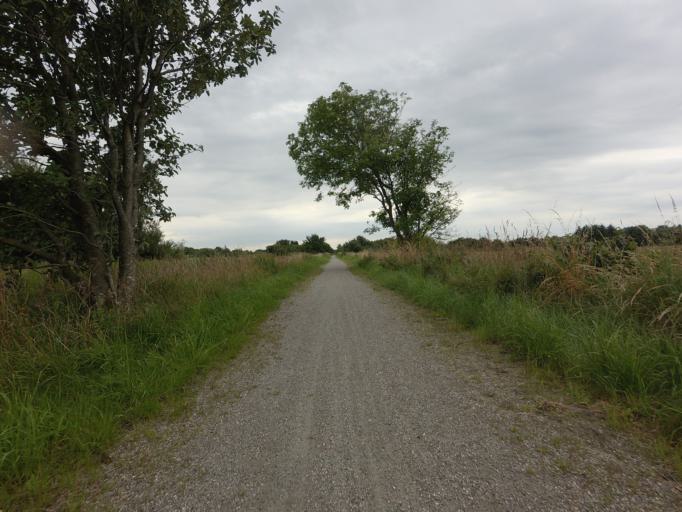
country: DK
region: North Denmark
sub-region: Alborg Kommune
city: Vadum
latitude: 57.0981
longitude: 9.8942
